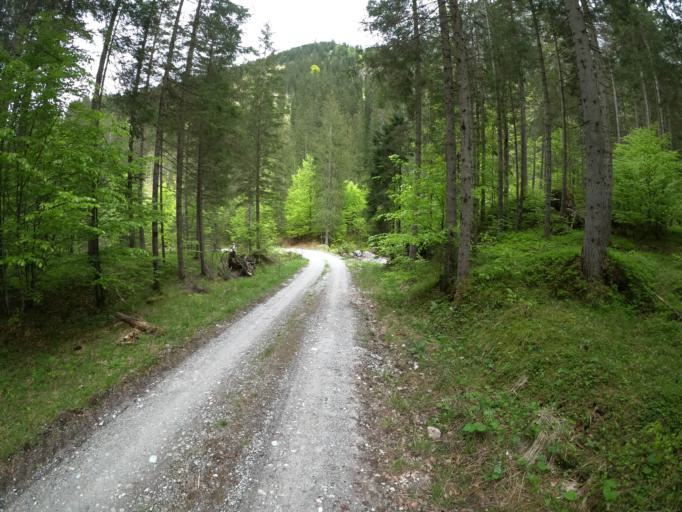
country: AT
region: Salzburg
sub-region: Politischer Bezirk Sankt Johann im Pongau
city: Werfen
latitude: 47.4665
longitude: 13.0817
